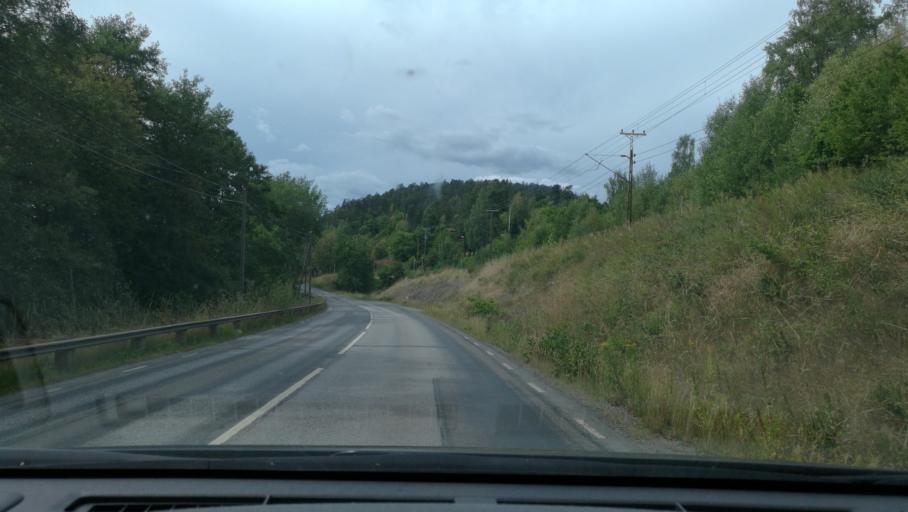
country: SE
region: OEstergoetland
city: Lindo
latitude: 58.6659
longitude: 16.2466
